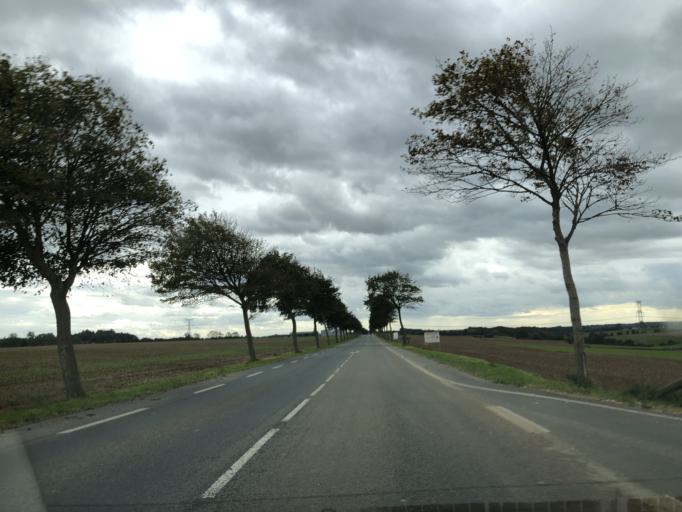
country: FR
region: Nord-Pas-de-Calais
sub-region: Departement du Pas-de-Calais
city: Fruges
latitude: 50.4780
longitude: 2.1162
